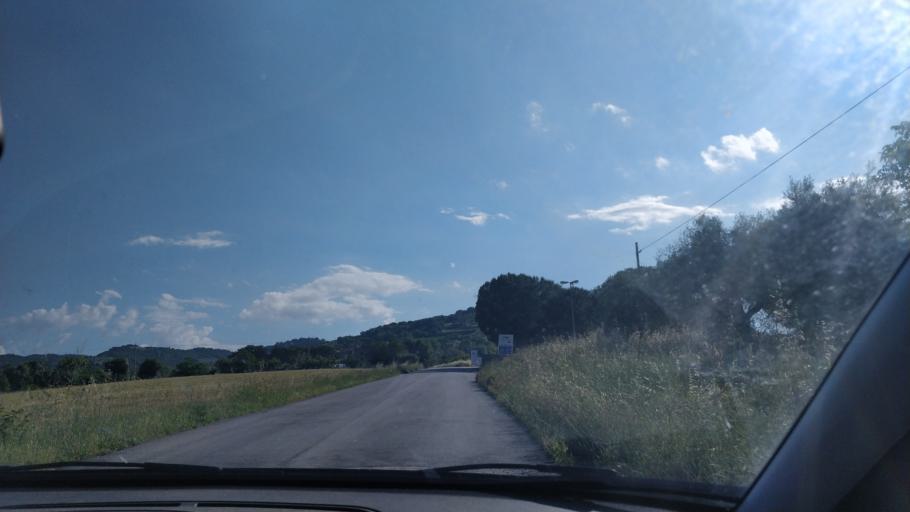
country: IT
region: The Marches
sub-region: Provincia di Ascoli Piceno
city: Massignano
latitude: 43.0322
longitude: 13.7962
